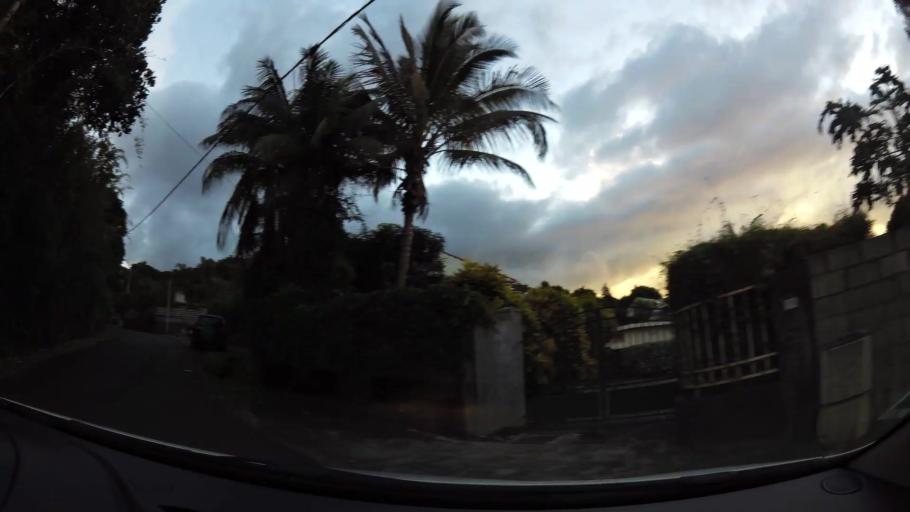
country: RE
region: Reunion
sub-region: Reunion
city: Saint-Denis
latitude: -20.9124
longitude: 55.4599
